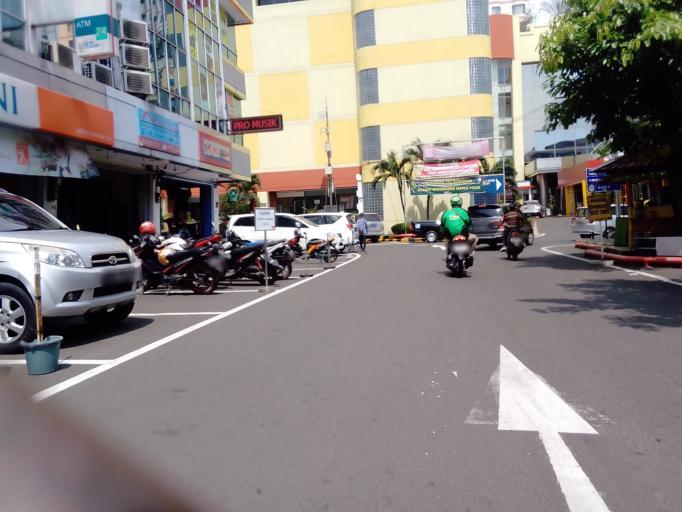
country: ID
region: Jakarta Raya
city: Jakarta
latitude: -6.1385
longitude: 106.8289
